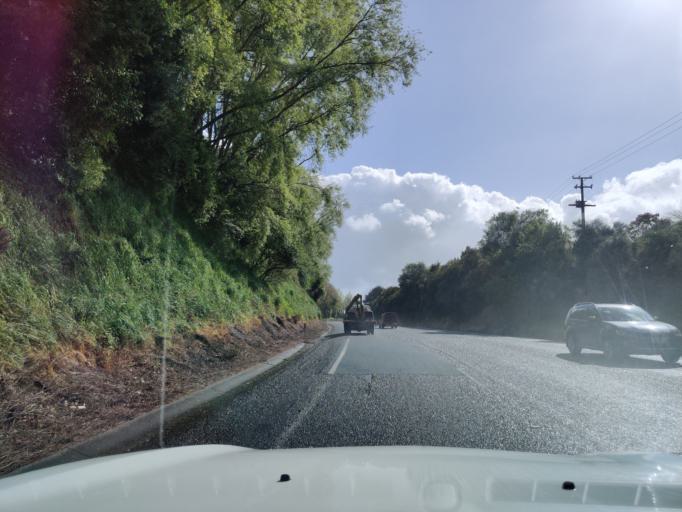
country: NZ
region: Waikato
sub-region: Matamata-Piako District
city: Matamata
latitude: -37.9462
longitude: 175.6567
